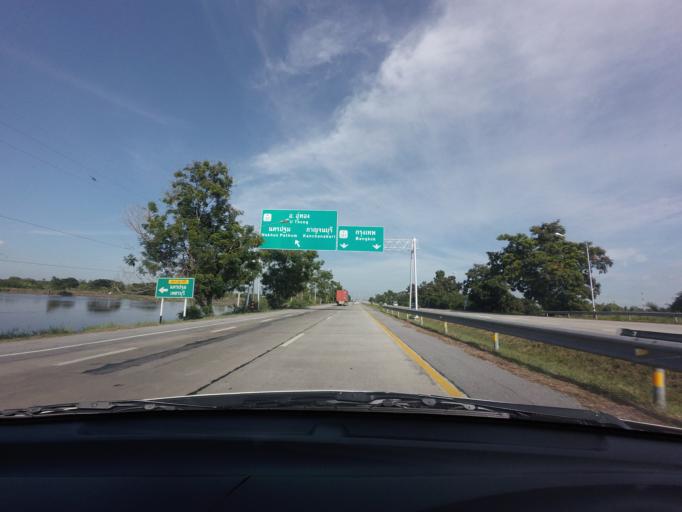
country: TH
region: Suphan Buri
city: Suphan Buri
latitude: 14.4681
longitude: 100.0420
